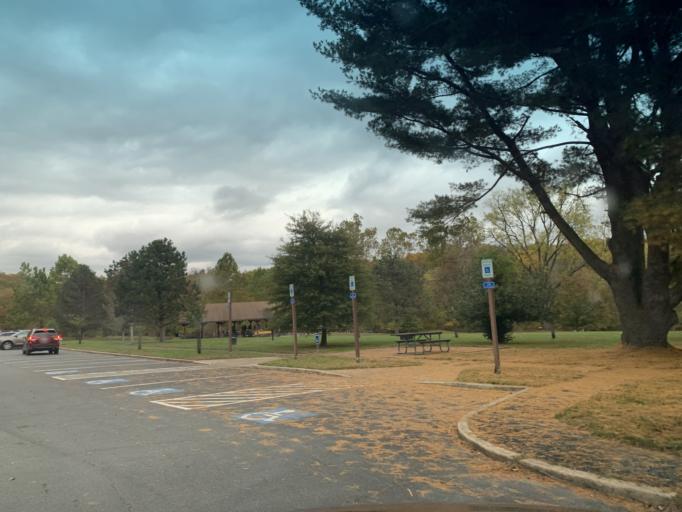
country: US
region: Maryland
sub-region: Harford County
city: Havre de Grace
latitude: 39.6204
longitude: -76.1590
